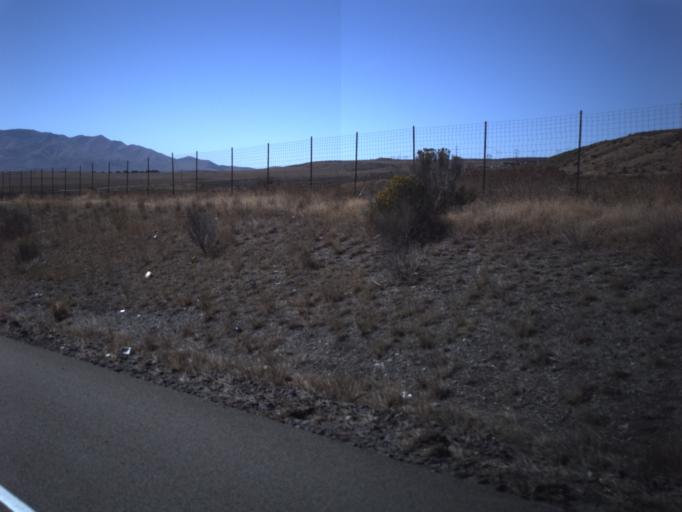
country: US
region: Utah
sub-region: Salt Lake County
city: Bluffdale
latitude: 40.4279
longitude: -111.9275
